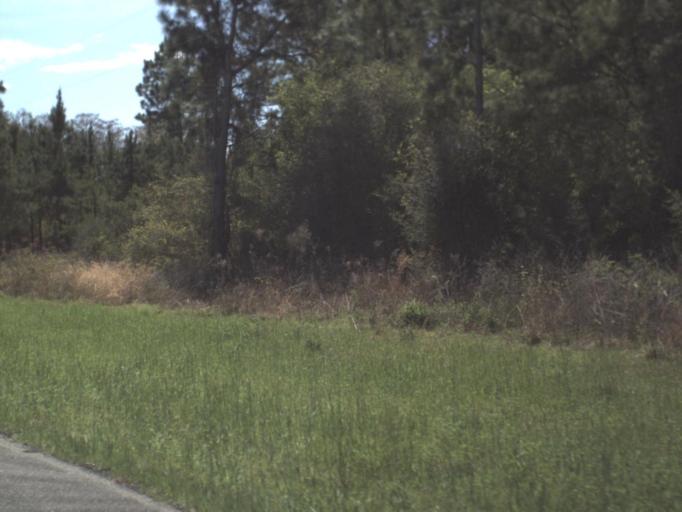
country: US
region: Florida
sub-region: Walton County
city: DeFuniak Springs
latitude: 30.8168
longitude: -85.9583
